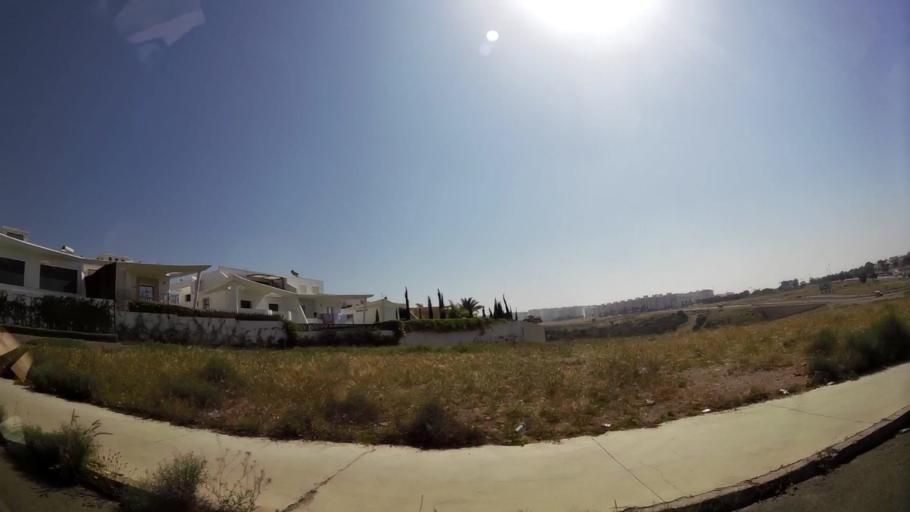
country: MA
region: Souss-Massa-Draa
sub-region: Agadir-Ida-ou-Tnan
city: Agadir
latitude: 30.4372
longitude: -9.5803
